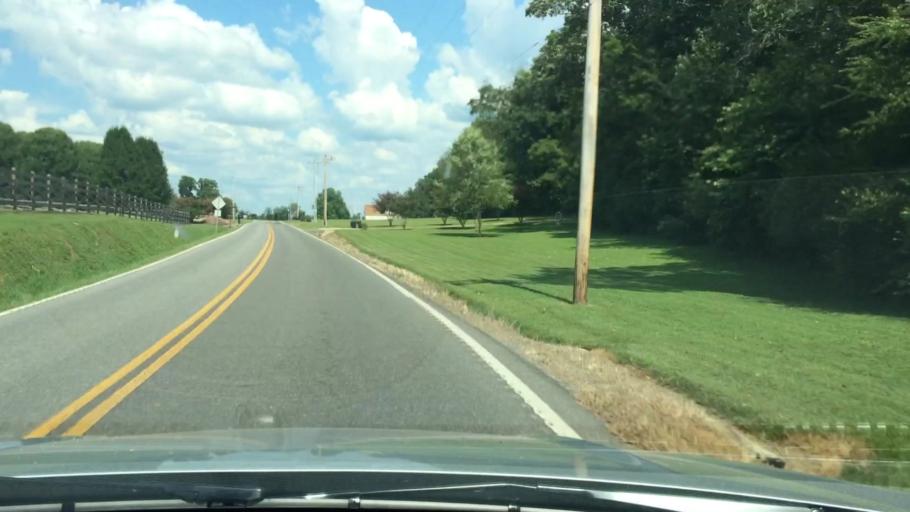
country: US
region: Tennessee
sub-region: McMinn County
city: Englewood
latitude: 35.4823
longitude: -84.5217
